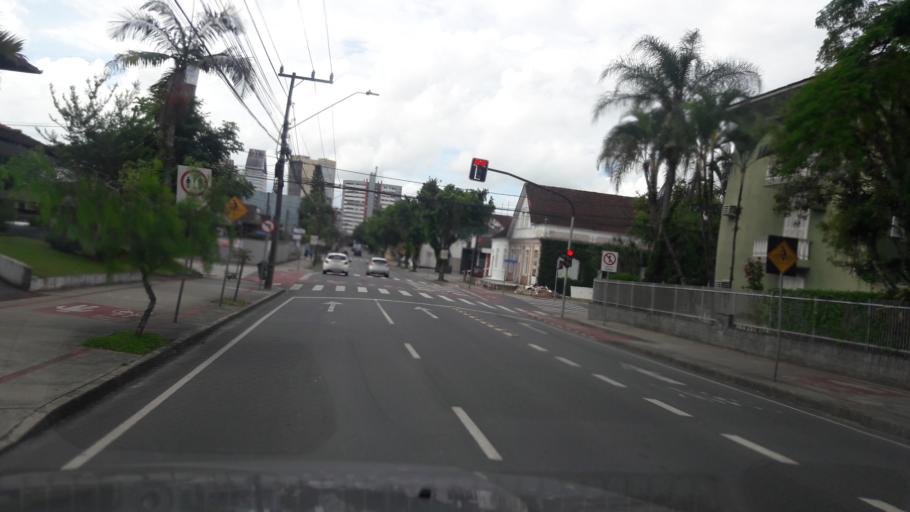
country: BR
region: Santa Catarina
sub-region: Joinville
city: Joinville
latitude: -26.3116
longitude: -48.8429
